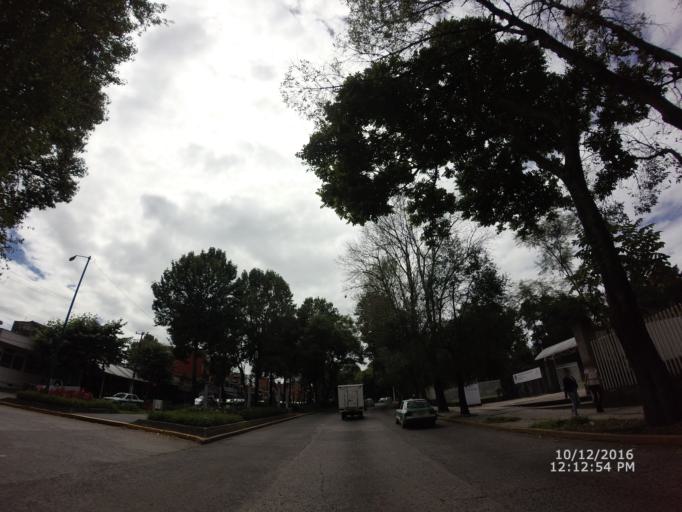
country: MX
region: Veracruz
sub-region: Xalapa
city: Xalapa de Enriquez
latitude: 19.5562
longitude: -96.9289
